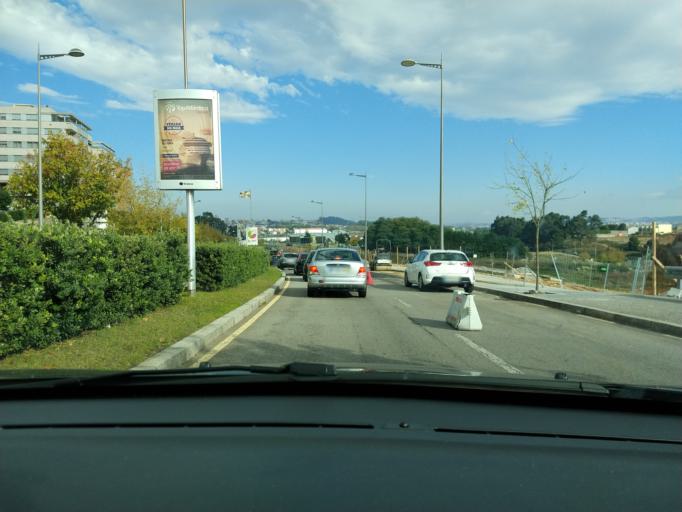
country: PT
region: Porto
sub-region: Vila Nova de Gaia
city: Oliveira do Douro
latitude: 41.1227
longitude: -8.5986
